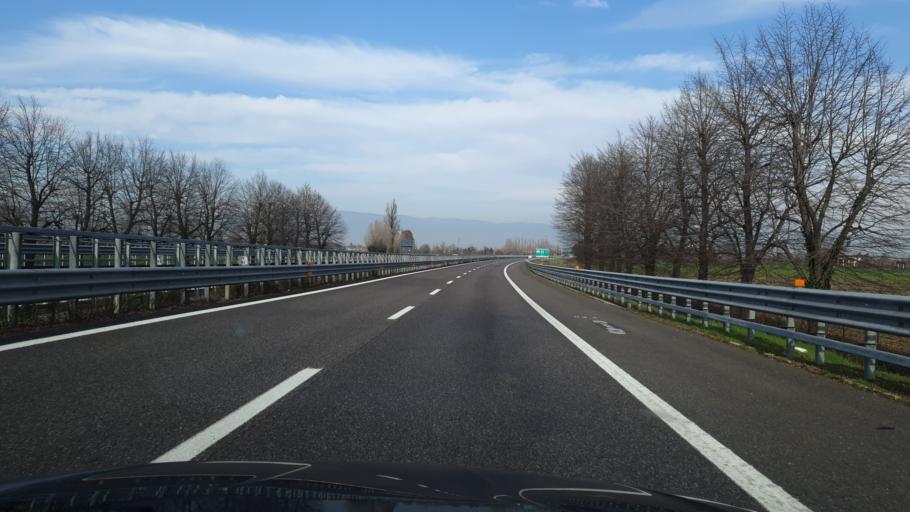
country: IT
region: Veneto
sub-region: Provincia di Vicenza
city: Lisiera
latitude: 45.5851
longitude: 11.5987
